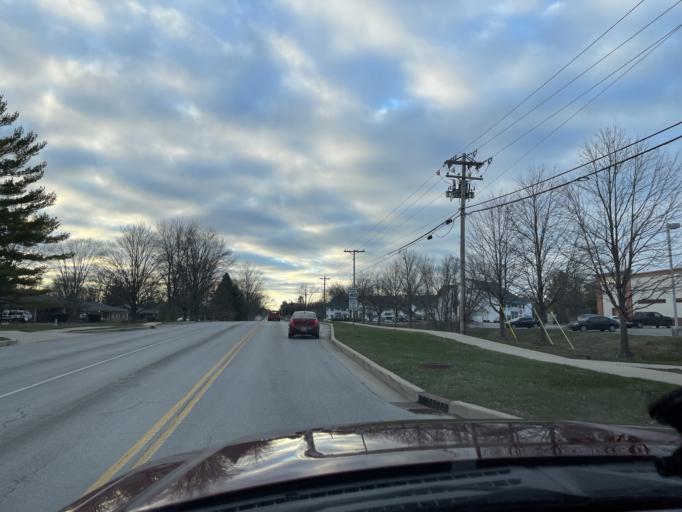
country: US
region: Indiana
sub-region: Hendricks County
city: Avon
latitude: 39.7774
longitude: -86.4002
